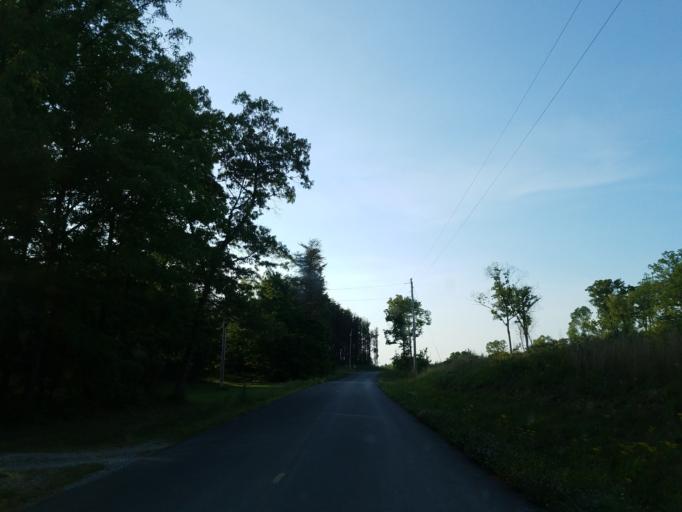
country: US
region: Georgia
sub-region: Whitfield County
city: Dalton
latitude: 34.6673
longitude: -85.0792
